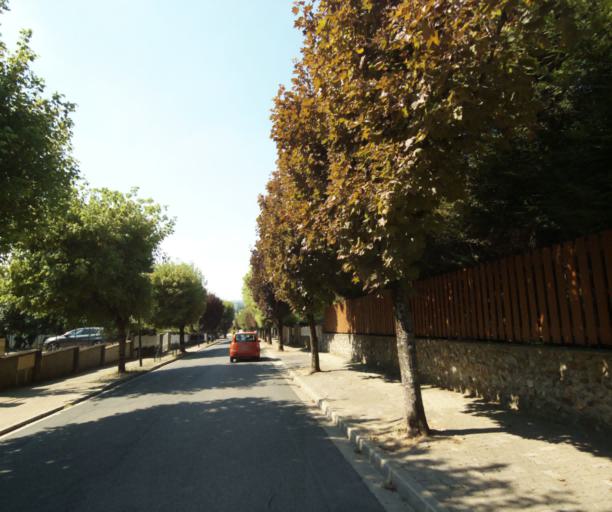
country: FR
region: Ile-de-France
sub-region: Departement de Seine-et-Marne
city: Saint-Thibault-des-Vignes
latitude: 48.8690
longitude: 2.6869
